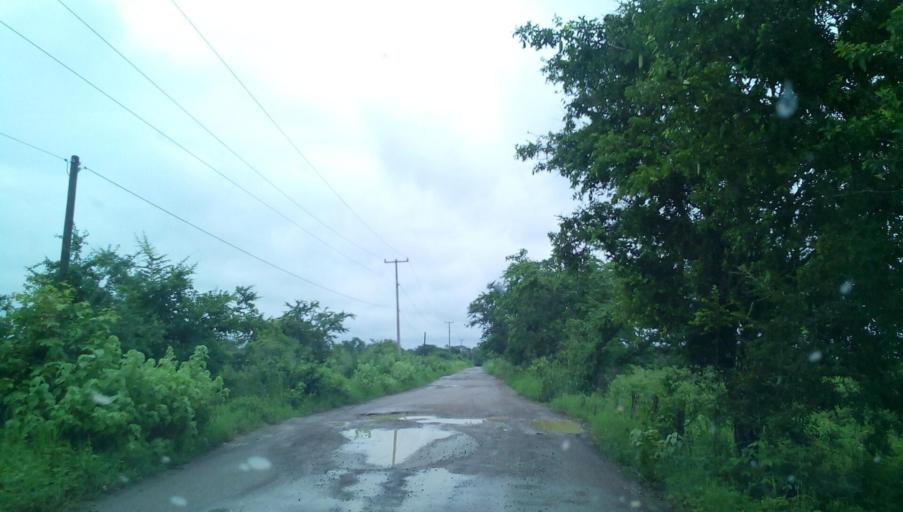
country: MX
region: Veracruz
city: Tempoal de Sanchez
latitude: 21.4858
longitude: -98.4172
